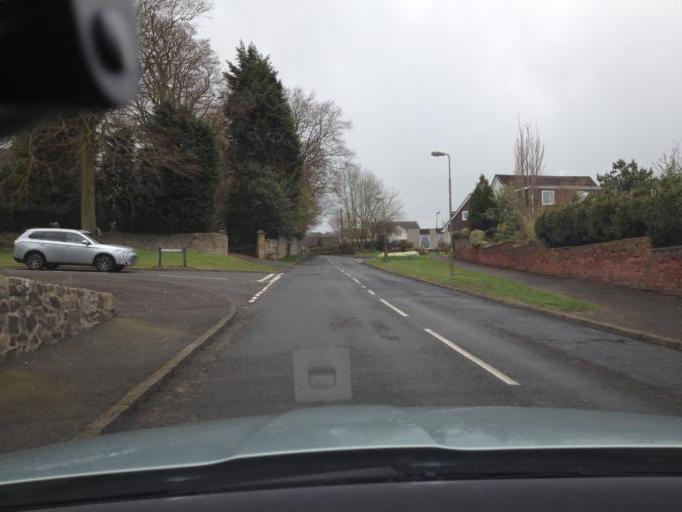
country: GB
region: Scotland
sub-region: West Lothian
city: Linlithgow
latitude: 55.9699
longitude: -3.5972
